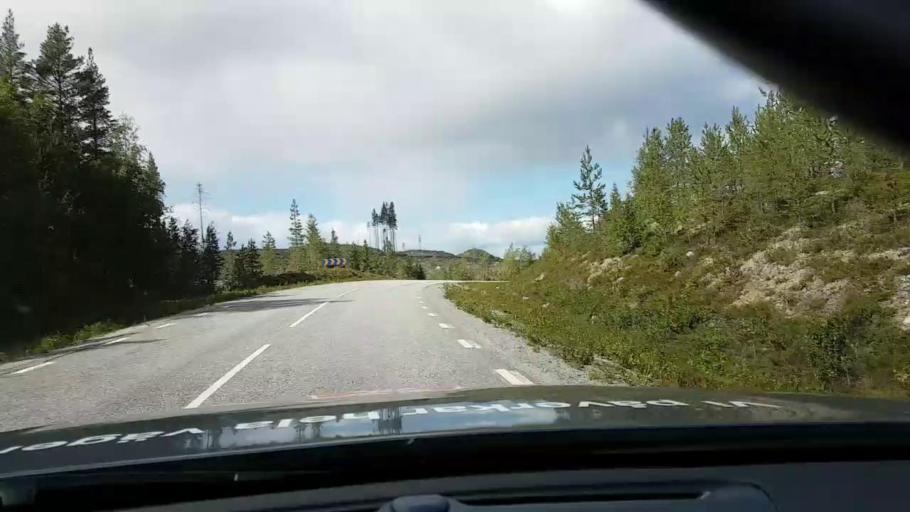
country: SE
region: Vaesternorrland
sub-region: OErnskoeldsviks Kommun
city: Bredbyn
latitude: 63.6765
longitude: 17.7927
